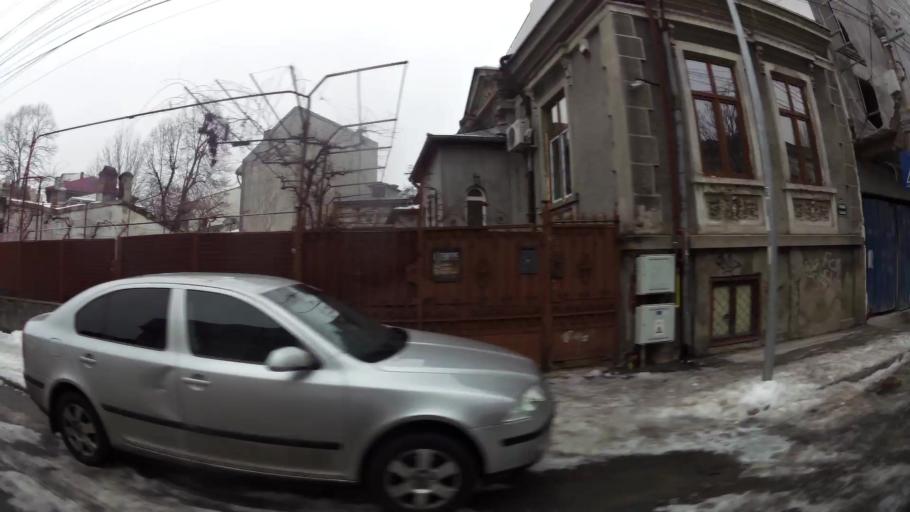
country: RO
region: Bucuresti
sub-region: Municipiul Bucuresti
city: Bucharest
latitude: 44.4438
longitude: 26.1081
